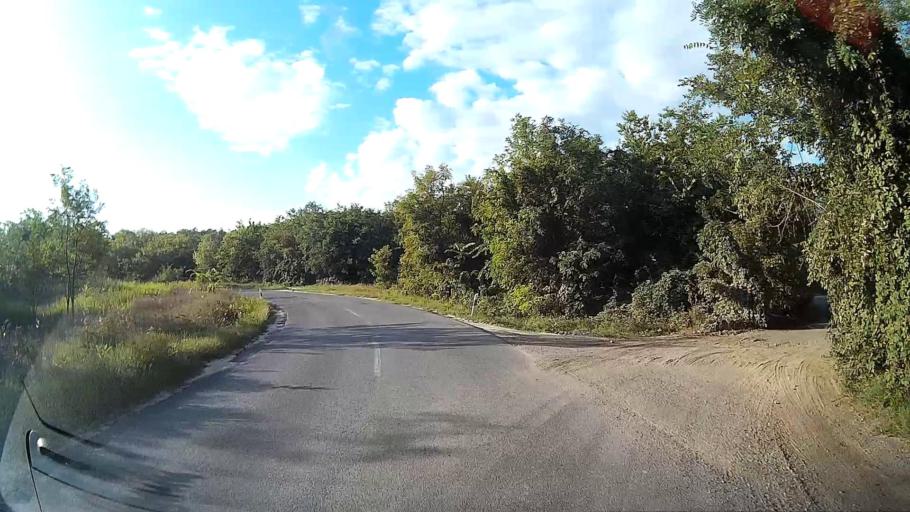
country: HU
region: Pest
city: Mogyorod
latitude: 47.5848
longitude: 19.2309
